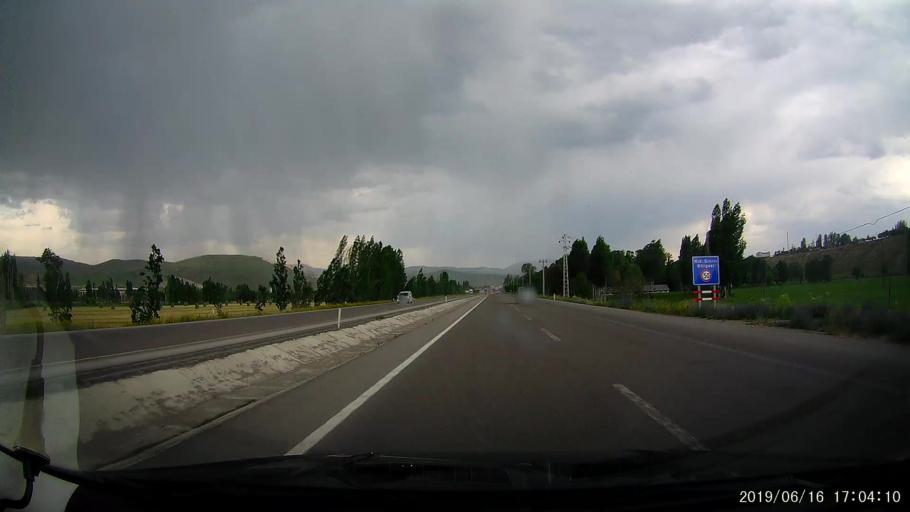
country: TR
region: Erzurum
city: Askale
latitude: 39.9287
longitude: 40.7149
